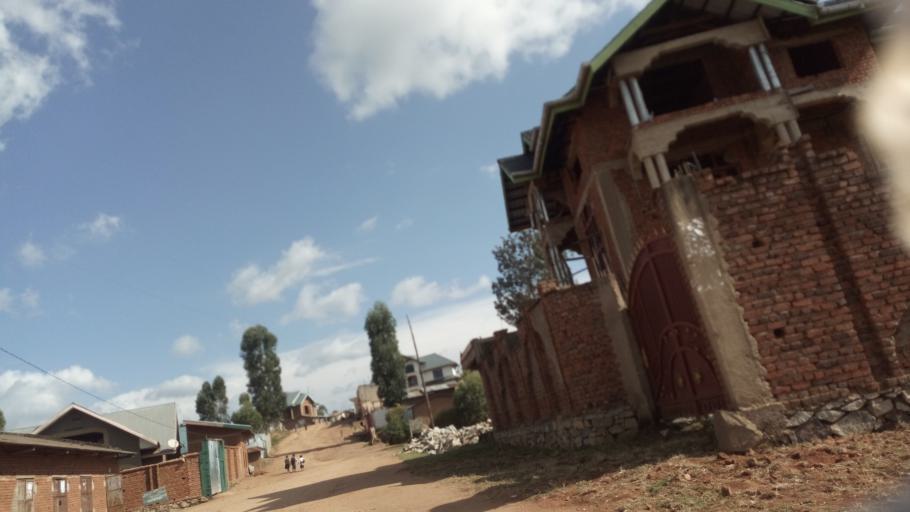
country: CD
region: Nord Kivu
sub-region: North Kivu
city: Butembo
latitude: 0.1103
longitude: 29.3239
